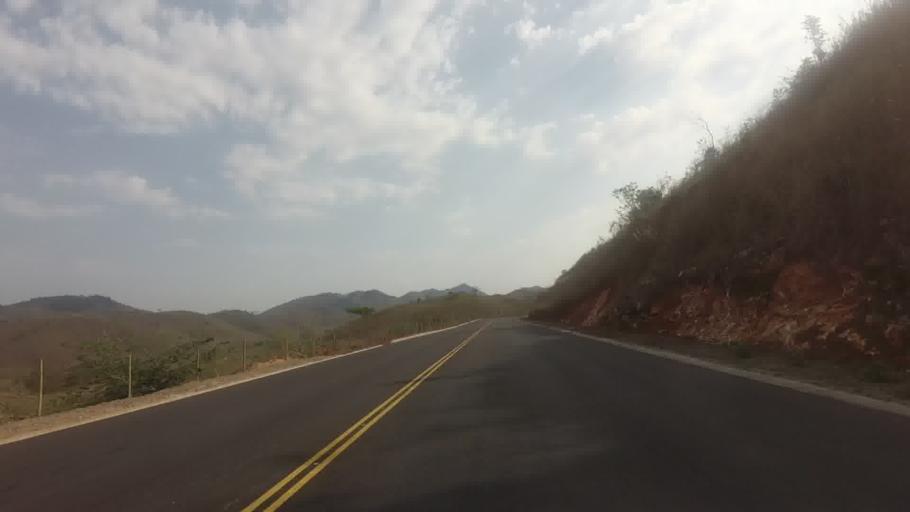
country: BR
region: Rio de Janeiro
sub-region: Itaperuna
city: Itaperuna
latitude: -21.2888
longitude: -41.8010
